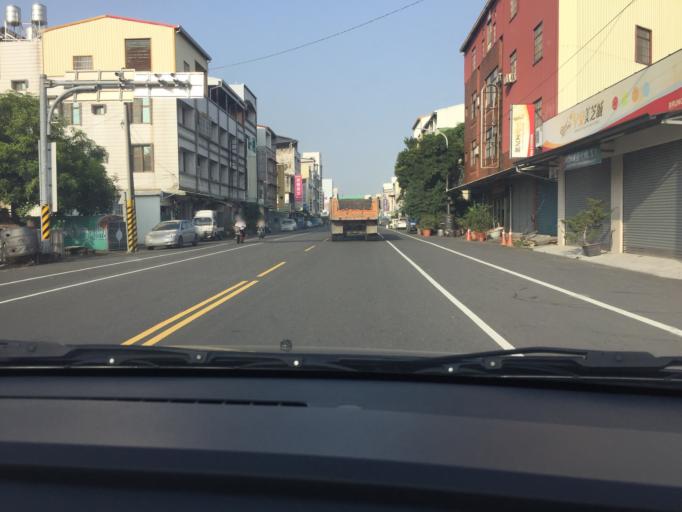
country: TW
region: Taiwan
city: Xinying
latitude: 23.1931
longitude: 120.3148
